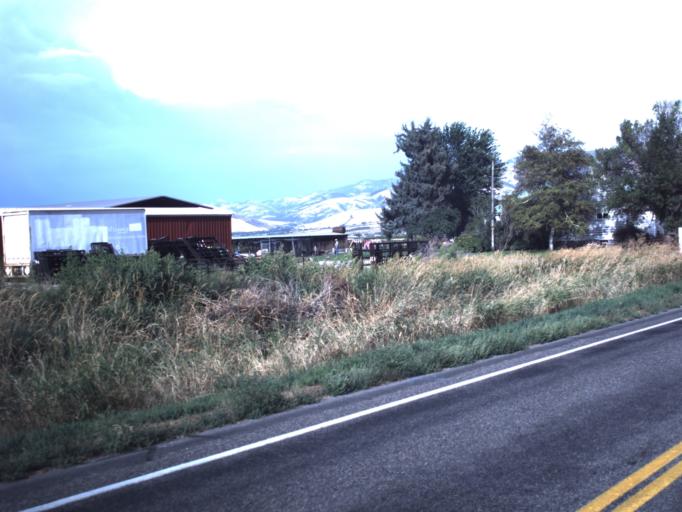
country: US
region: Utah
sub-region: Cache County
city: Lewiston
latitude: 41.9760
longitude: -111.8446
